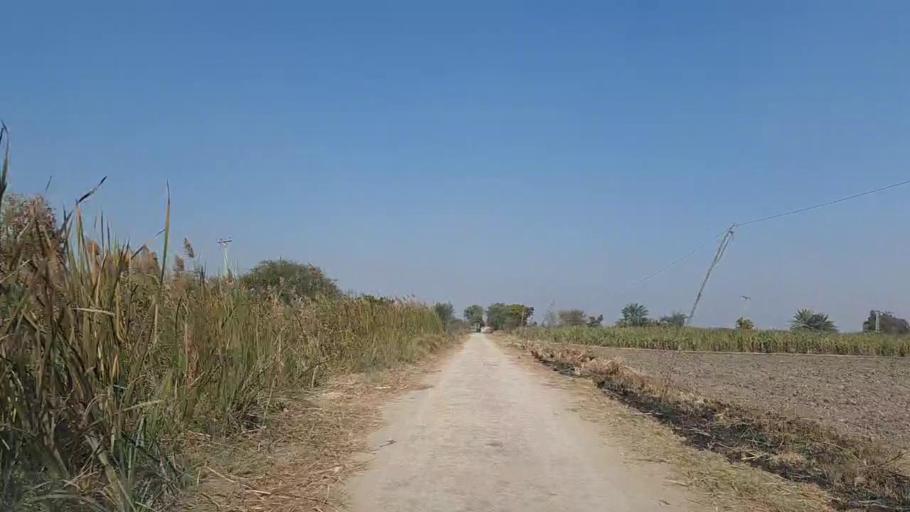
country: PK
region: Sindh
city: Daur
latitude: 26.5077
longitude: 68.3464
